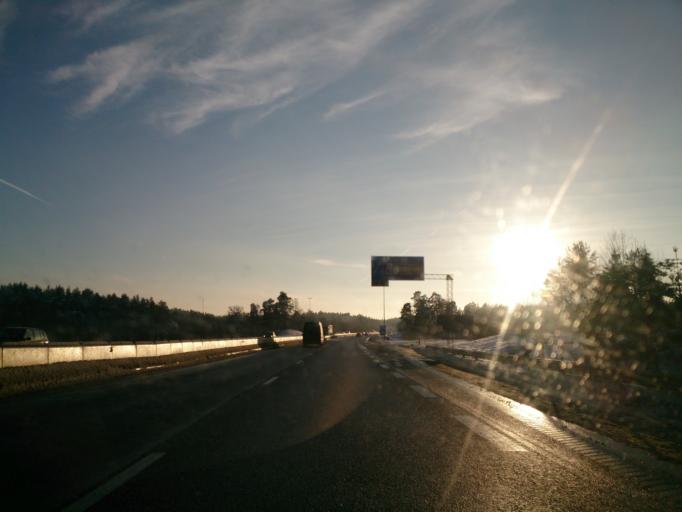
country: SE
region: OEstergoetland
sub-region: Norrkopings Kommun
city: Kimstad
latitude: 58.5540
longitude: 16.0564
